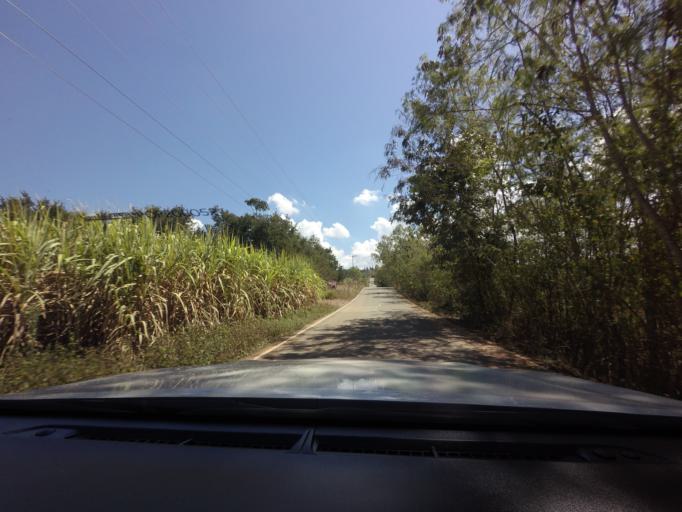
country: TH
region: Nakhon Ratchasima
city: Wang Nam Khiao
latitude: 14.4360
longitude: 101.7067
